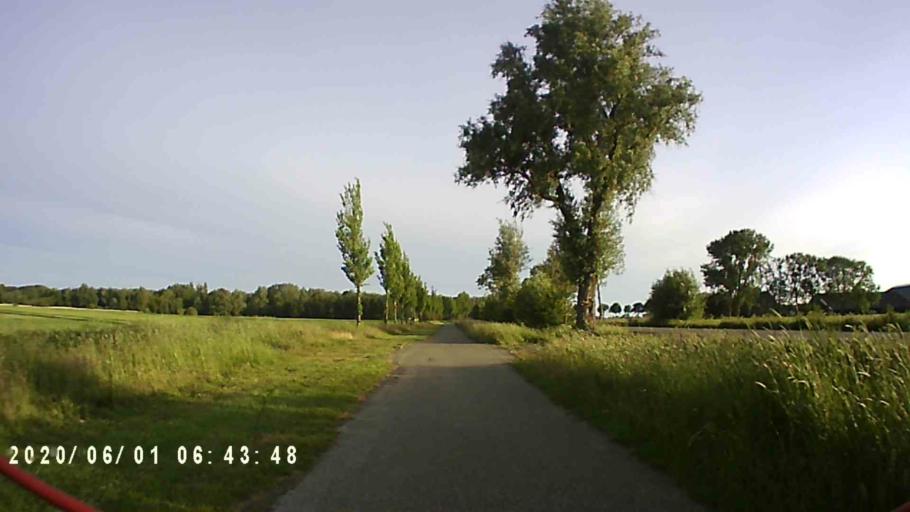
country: NL
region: Friesland
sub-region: Gemeente Kollumerland en Nieuwkruisland
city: Kollum
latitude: 53.2991
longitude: 6.1506
